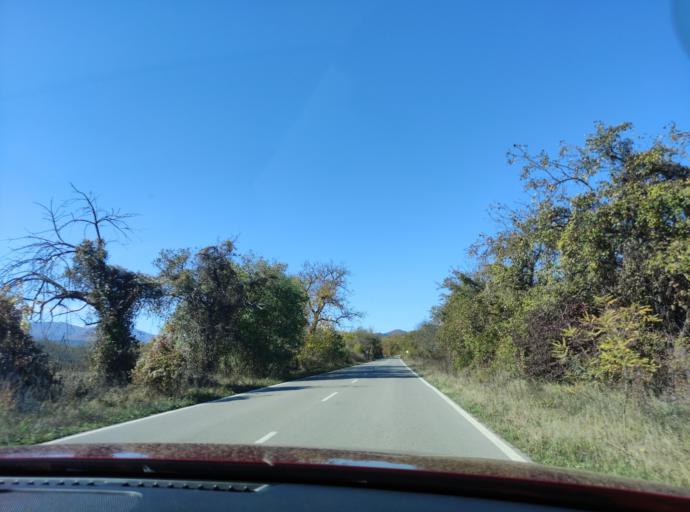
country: BG
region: Montana
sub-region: Obshtina Chiprovtsi
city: Chiprovtsi
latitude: 43.4140
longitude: 23.0394
